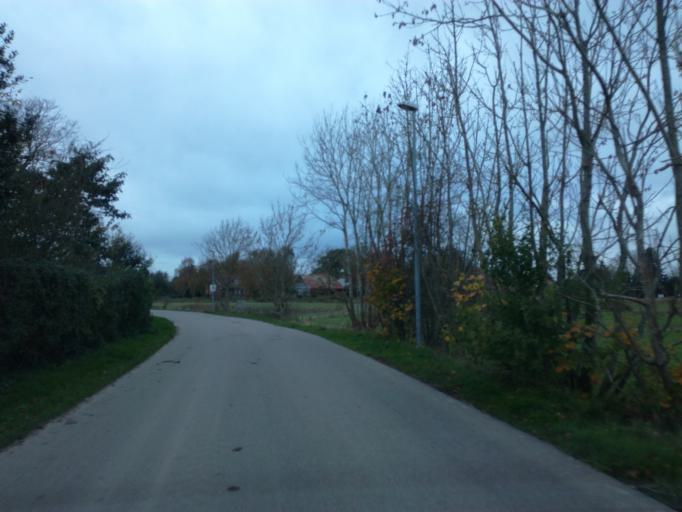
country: DK
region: South Denmark
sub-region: Fredericia Kommune
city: Fredericia
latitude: 55.6218
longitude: 9.7863
